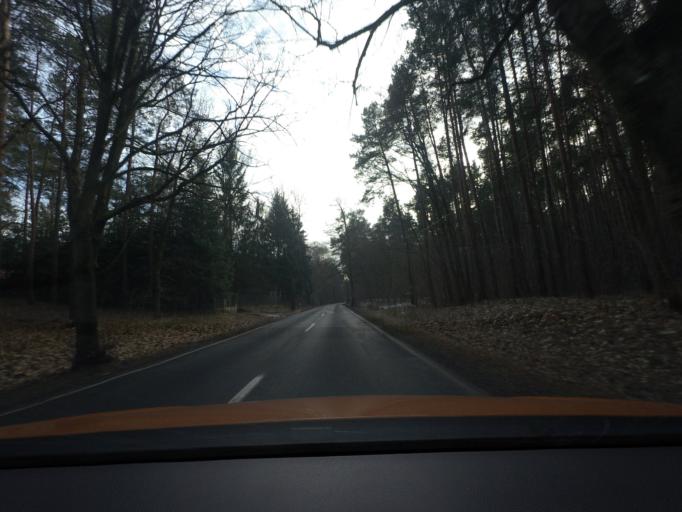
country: DE
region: Brandenburg
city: Wandlitz
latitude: 52.7442
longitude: 13.3724
